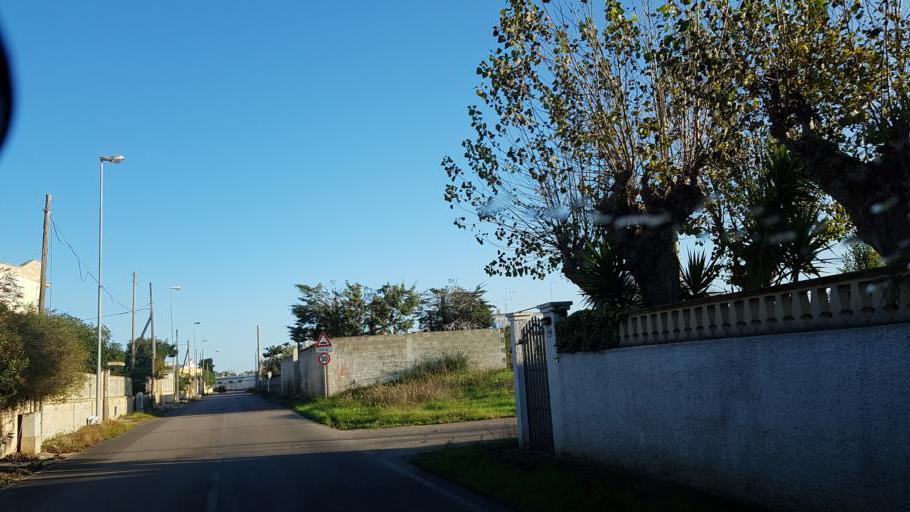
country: IT
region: Apulia
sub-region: Provincia di Brindisi
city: Torchiarolo
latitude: 40.5018
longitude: 18.1132
